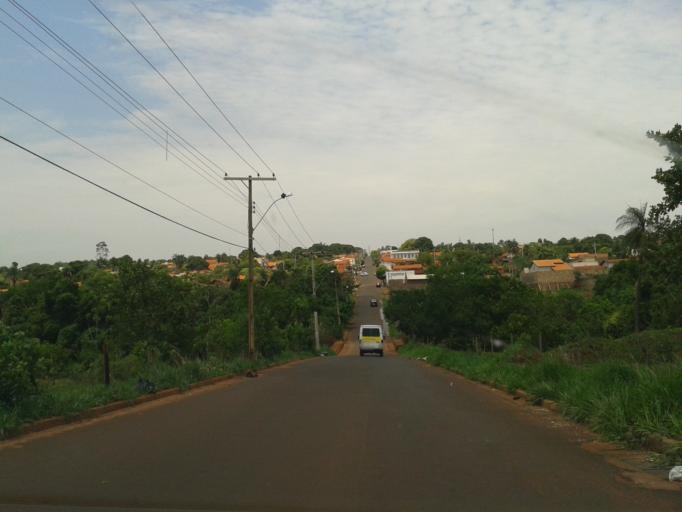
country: BR
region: Minas Gerais
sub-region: Ituiutaba
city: Ituiutaba
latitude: -18.9912
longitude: -49.4402
